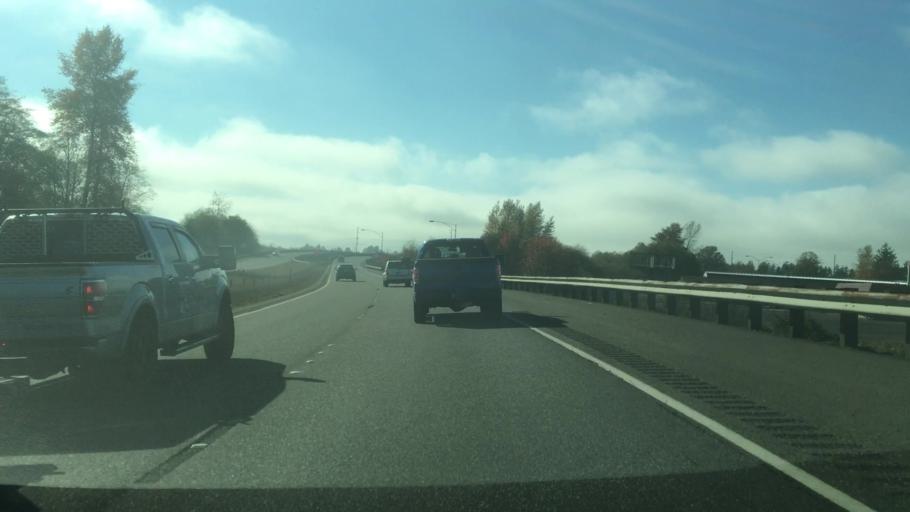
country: US
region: Washington
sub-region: Grays Harbor County
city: Montesano
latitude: 46.9781
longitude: -123.5950
